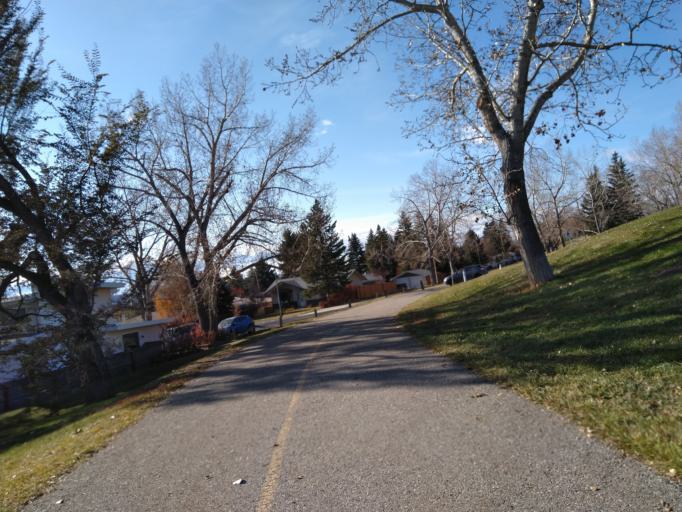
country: CA
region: Alberta
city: Calgary
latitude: 51.0916
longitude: -114.1062
